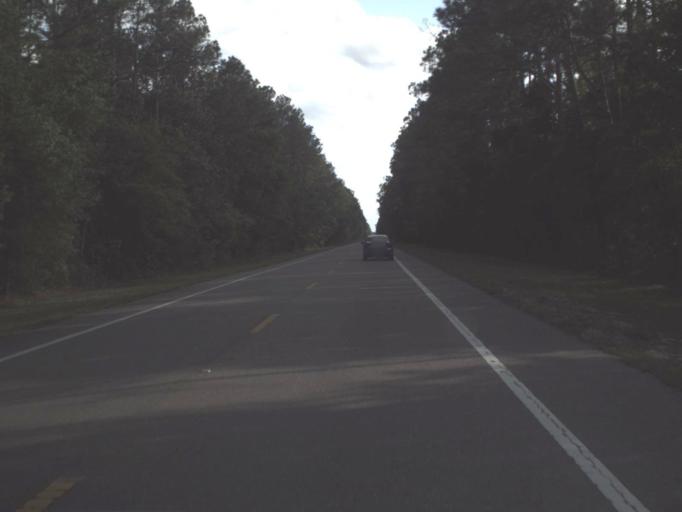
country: US
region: Florida
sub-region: Volusia County
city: Pierson
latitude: 29.3037
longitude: -81.3191
